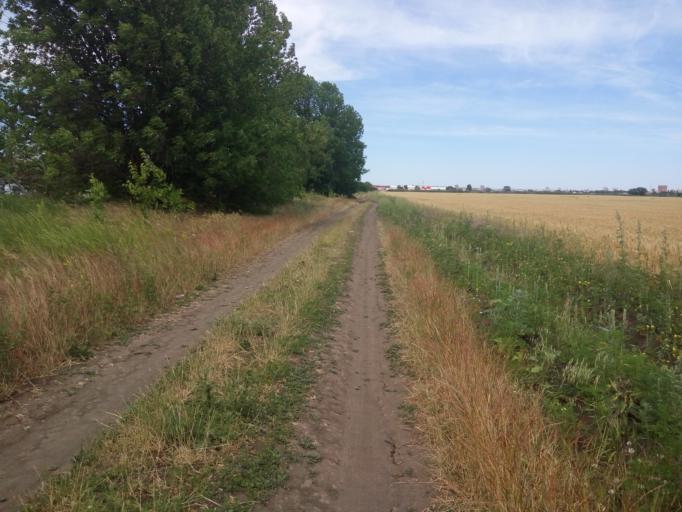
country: RU
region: Rostov
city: Bataysk
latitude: 47.1151
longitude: 39.7228
